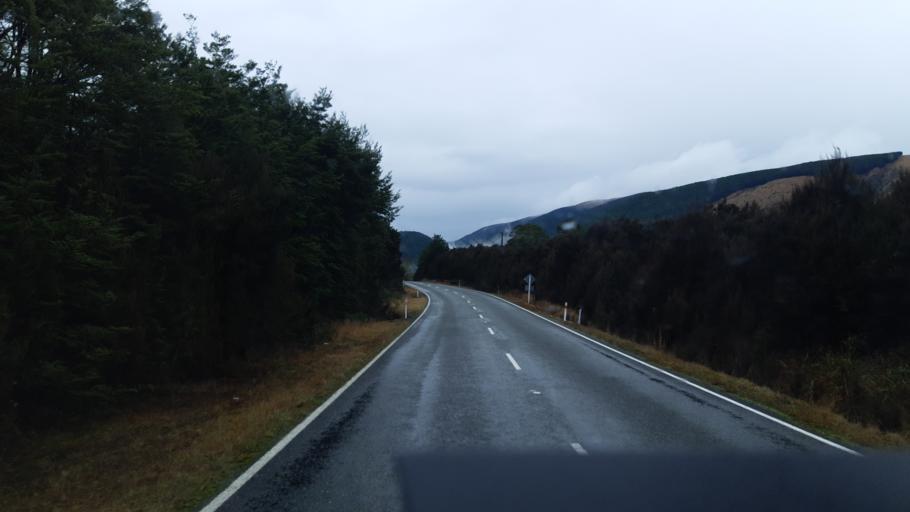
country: NZ
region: Tasman
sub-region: Tasman District
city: Wakefield
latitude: -41.7738
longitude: 172.8913
